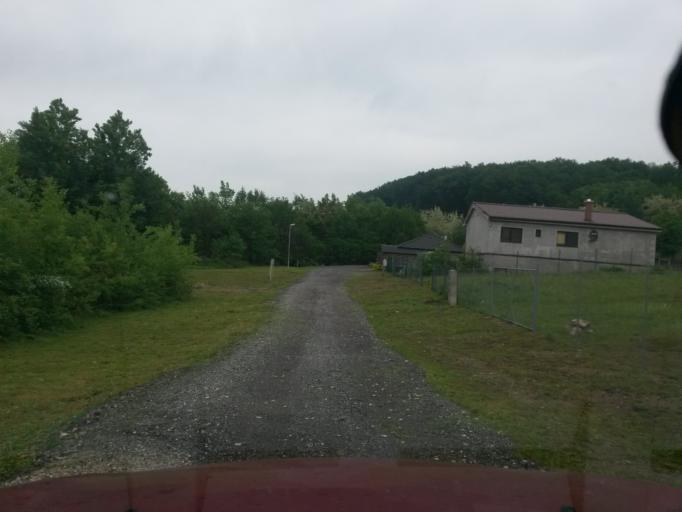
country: SK
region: Kosicky
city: Moldava nad Bodvou
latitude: 48.6950
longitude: 21.0726
